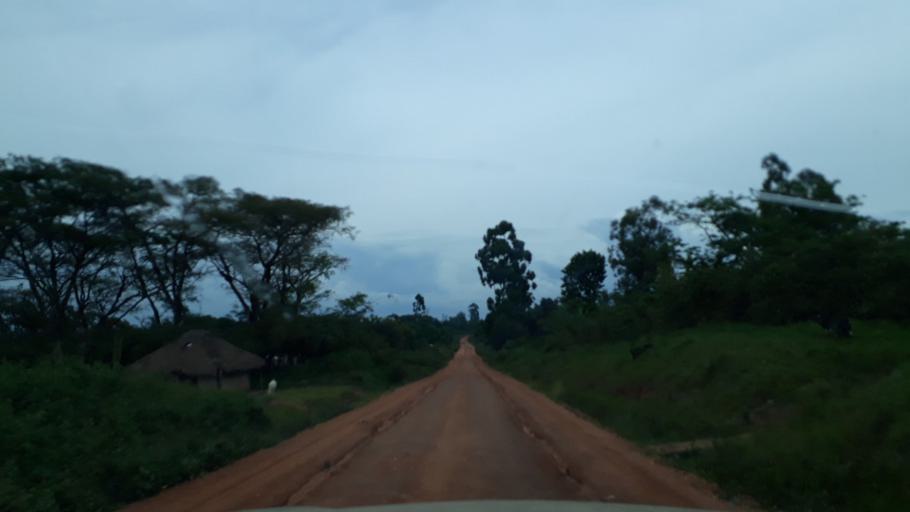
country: UG
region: Northern Region
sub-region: Zombo District
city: Paidha
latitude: 2.2058
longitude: 30.7514
